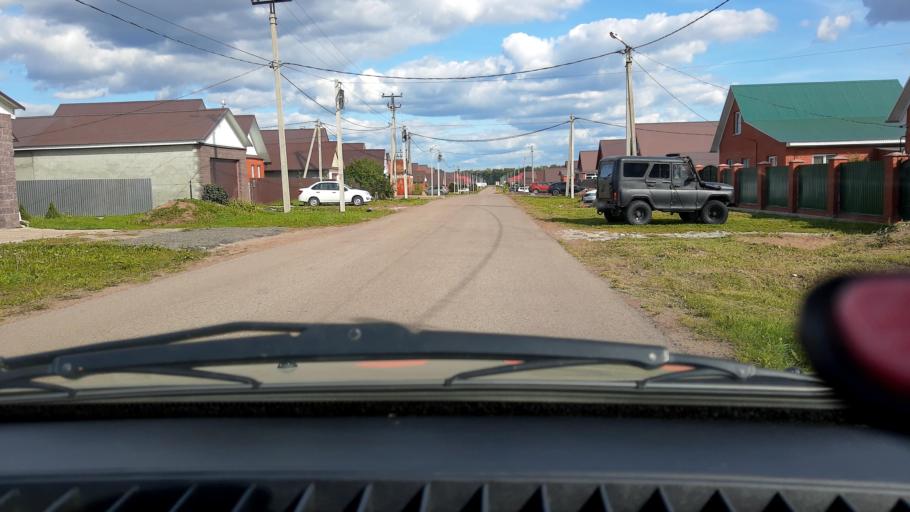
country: RU
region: Bashkortostan
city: Iglino
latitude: 54.7859
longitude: 56.2712
